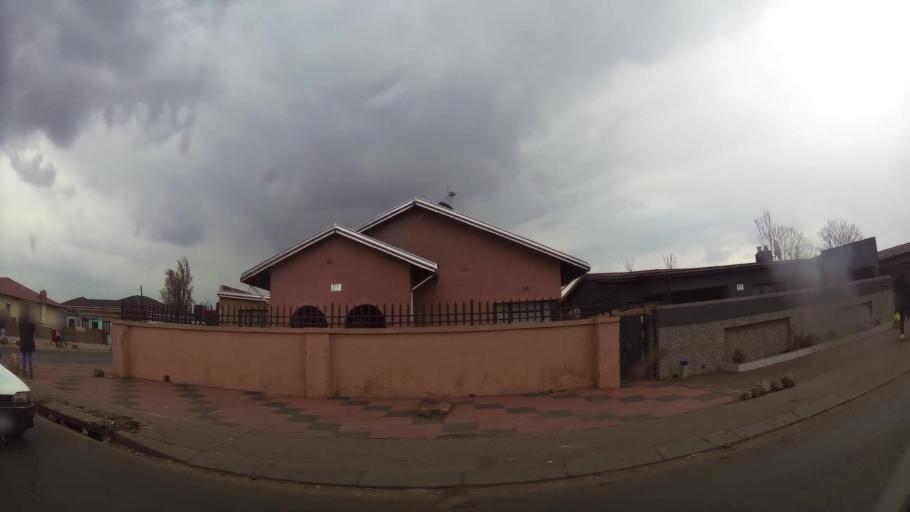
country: ZA
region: Gauteng
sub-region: Ekurhuleni Metropolitan Municipality
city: Germiston
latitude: -26.3259
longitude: 28.1533
